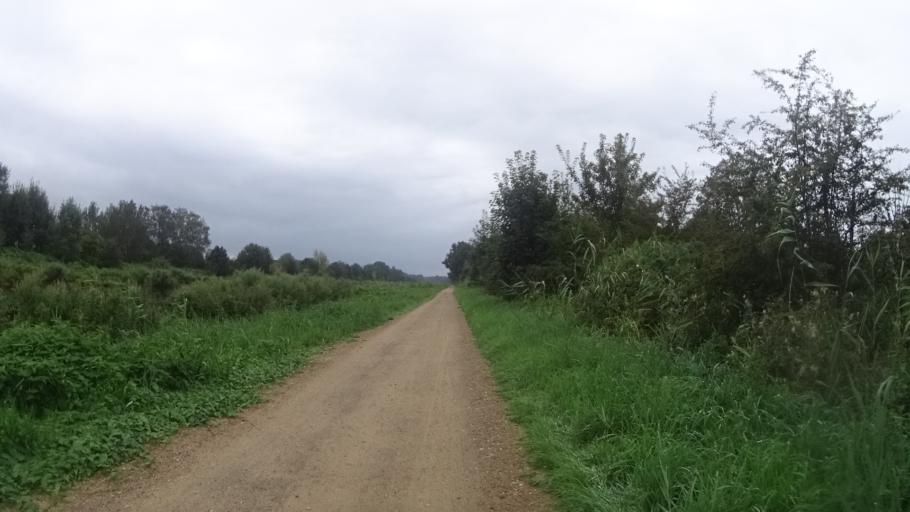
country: DE
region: Schleswig-Holstein
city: Witzeeze
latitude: 53.4451
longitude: 10.6196
